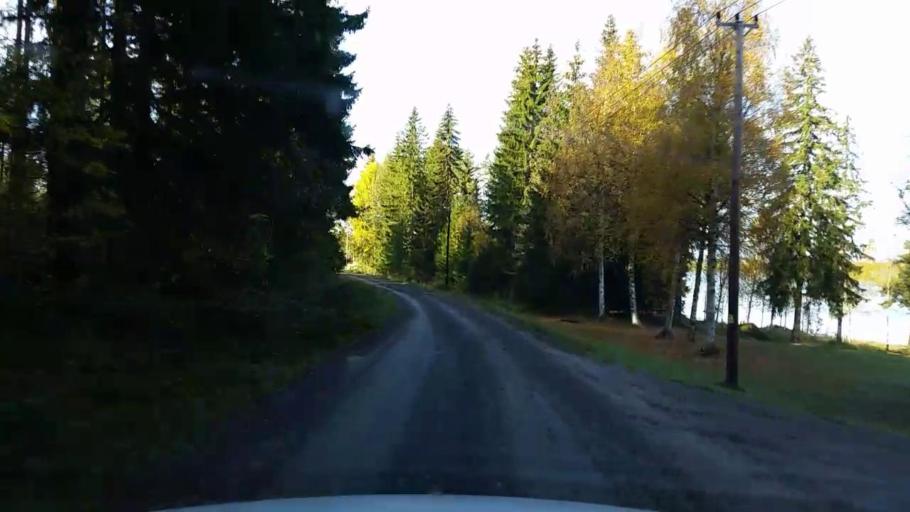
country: SE
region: Gaevleborg
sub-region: Ljusdals Kommun
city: Jaervsoe
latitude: 61.7904
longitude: 16.1839
